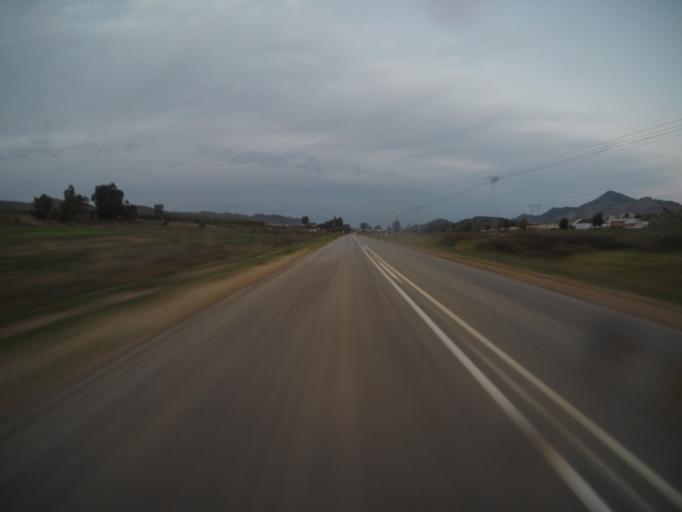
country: ZA
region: Western Cape
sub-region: Eden District Municipality
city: Plettenberg Bay
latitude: -33.8116
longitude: 23.7290
